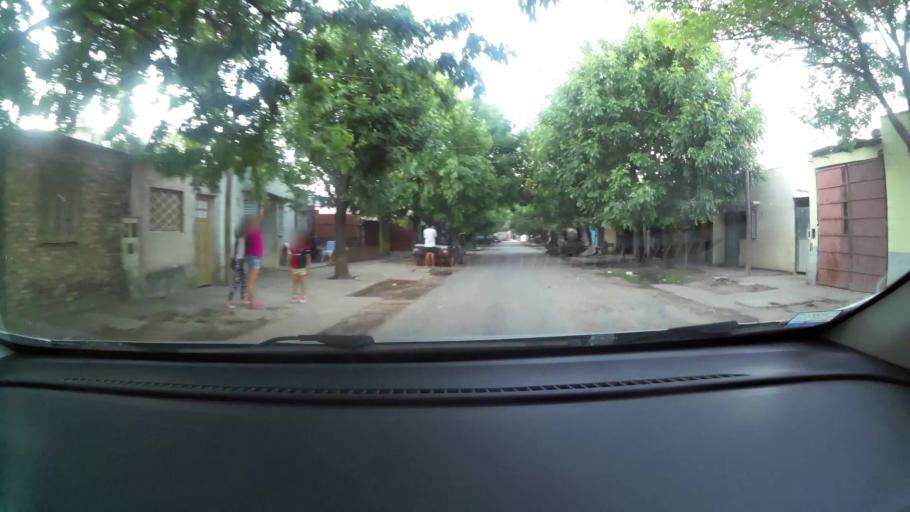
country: AR
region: Santa Fe
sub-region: Departamento de Rosario
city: Rosario
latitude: -32.9659
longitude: -60.6908
